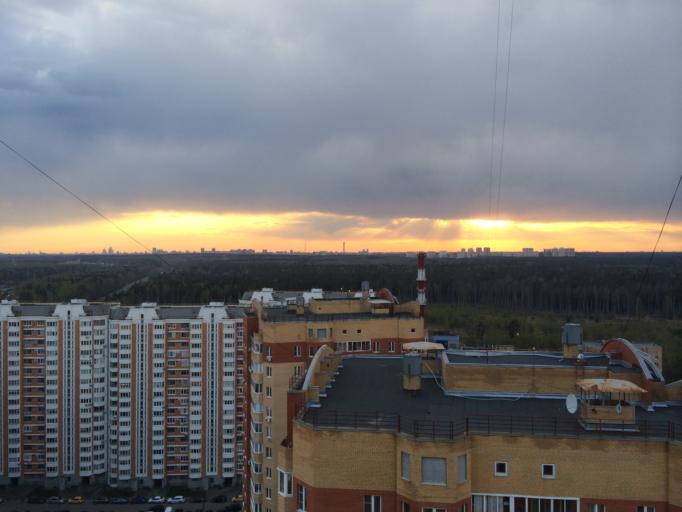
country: RU
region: Moskovskaya
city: Balashikha
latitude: 55.8084
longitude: 37.9434
